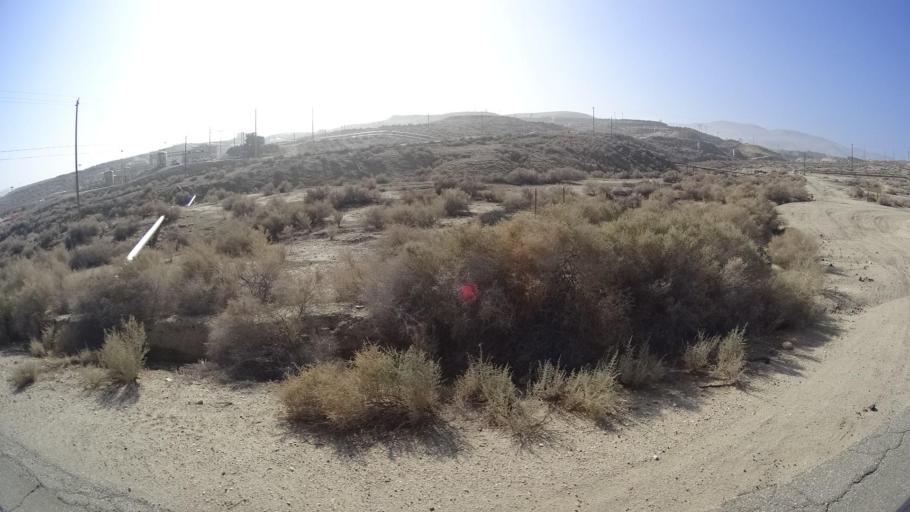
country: US
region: California
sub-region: Kern County
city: Taft Heights
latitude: 35.1442
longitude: -119.5093
